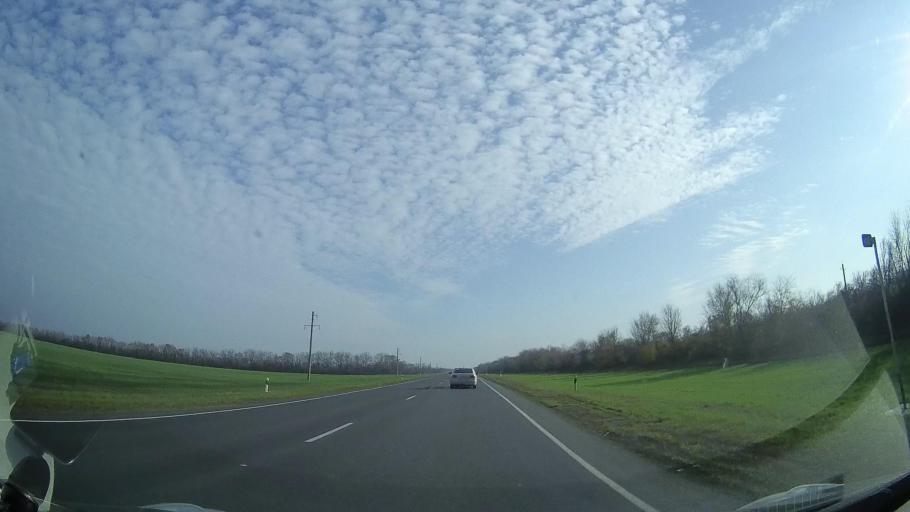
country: RU
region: Rostov
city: Gigant
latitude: 46.5284
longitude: 41.1995
